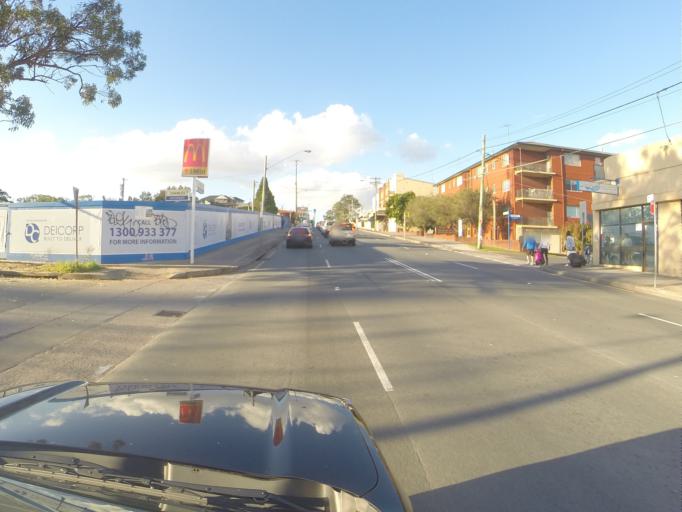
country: AU
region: New South Wales
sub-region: Canterbury
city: Canterbury
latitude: -33.9129
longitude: 151.1179
